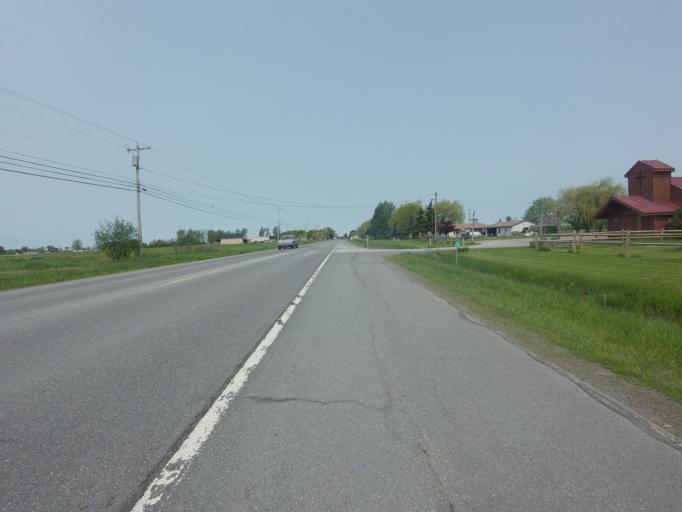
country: US
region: New York
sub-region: Jefferson County
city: Dexter
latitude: 44.0590
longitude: -76.1158
